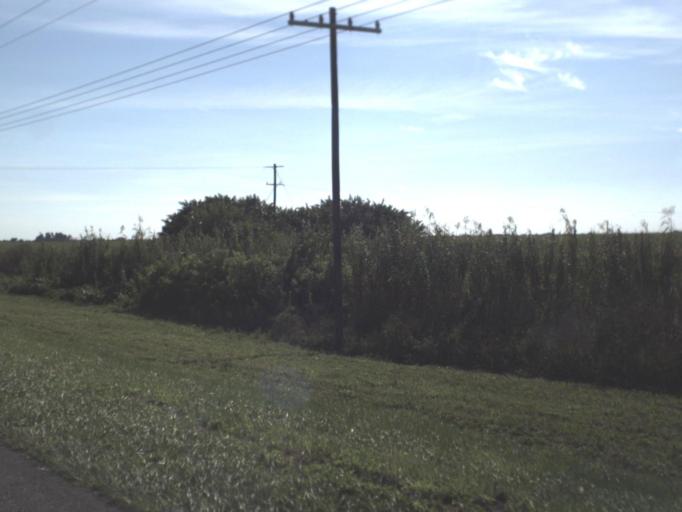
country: US
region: Florida
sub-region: Glades County
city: Moore Haven
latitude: 26.7946
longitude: -81.0829
